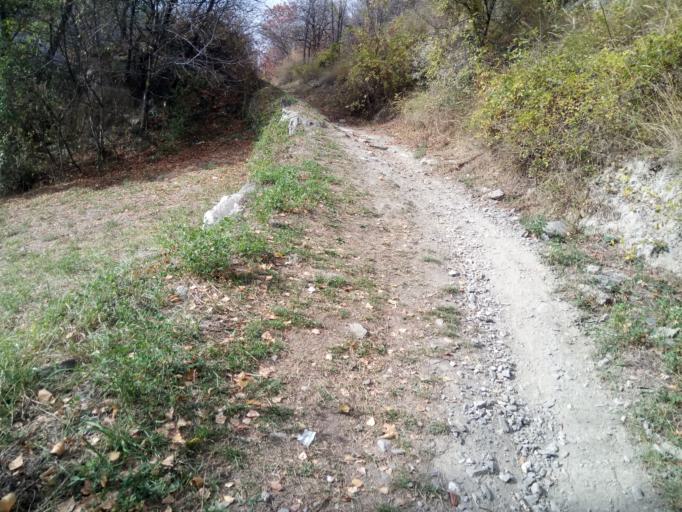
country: FR
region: Rhone-Alpes
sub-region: Departement de la Savoie
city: Villargondran
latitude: 45.2576
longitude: 6.4089
